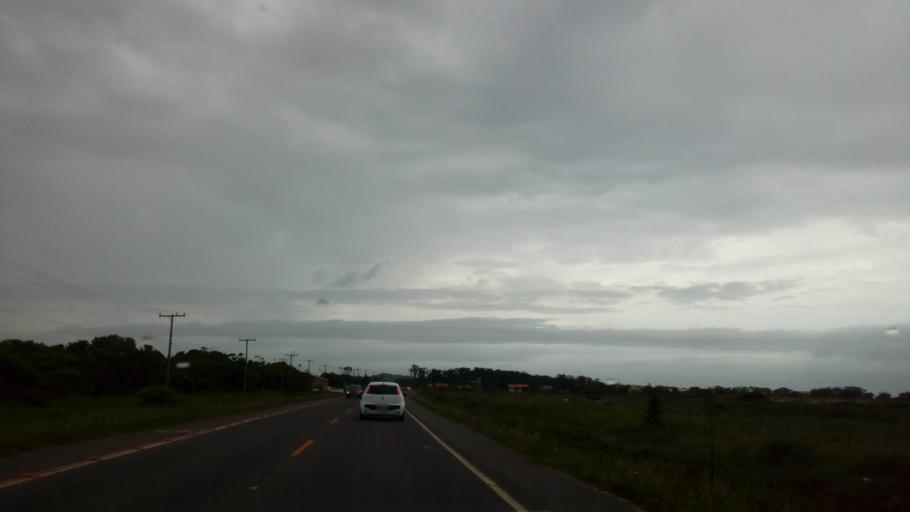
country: BR
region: Santa Catarina
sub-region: Laguna
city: Laguna
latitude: -28.5536
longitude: -48.8001
